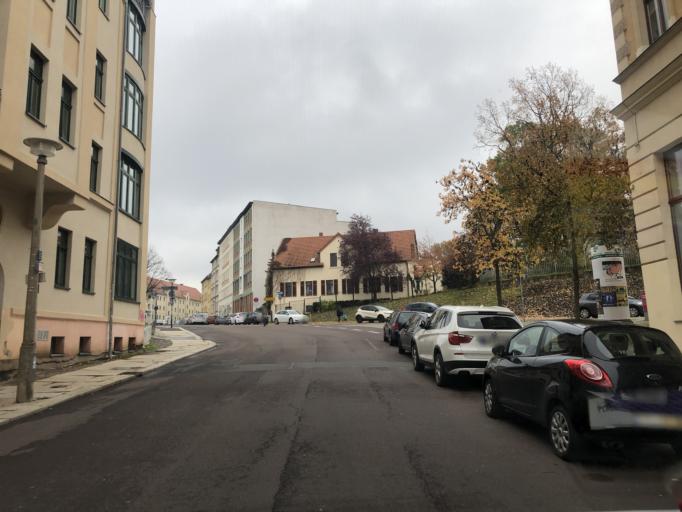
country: DE
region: Saxony-Anhalt
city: Halle (Saale)
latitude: 51.4719
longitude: 11.9713
